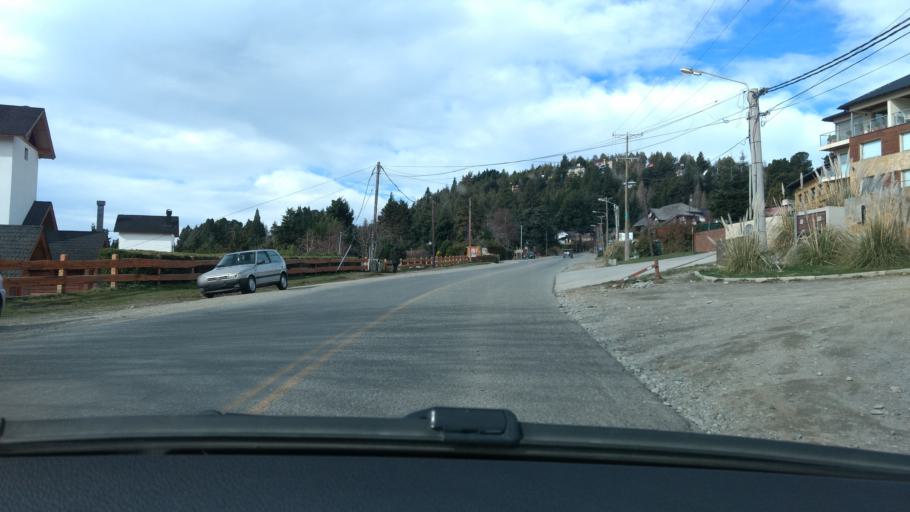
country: AR
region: Rio Negro
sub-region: Departamento de Bariloche
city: San Carlos de Bariloche
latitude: -41.1215
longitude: -71.3967
